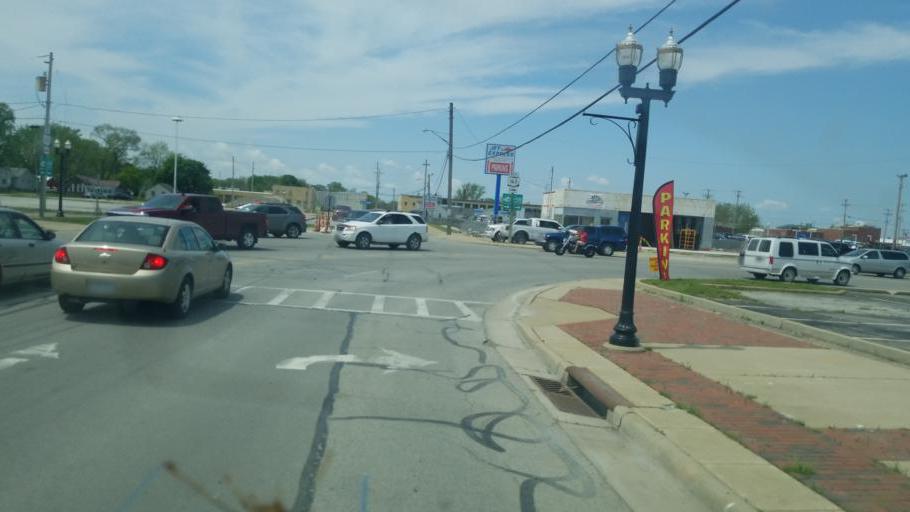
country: US
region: Ohio
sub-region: Ottawa County
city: Port Clinton
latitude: 41.5134
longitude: -82.9426
